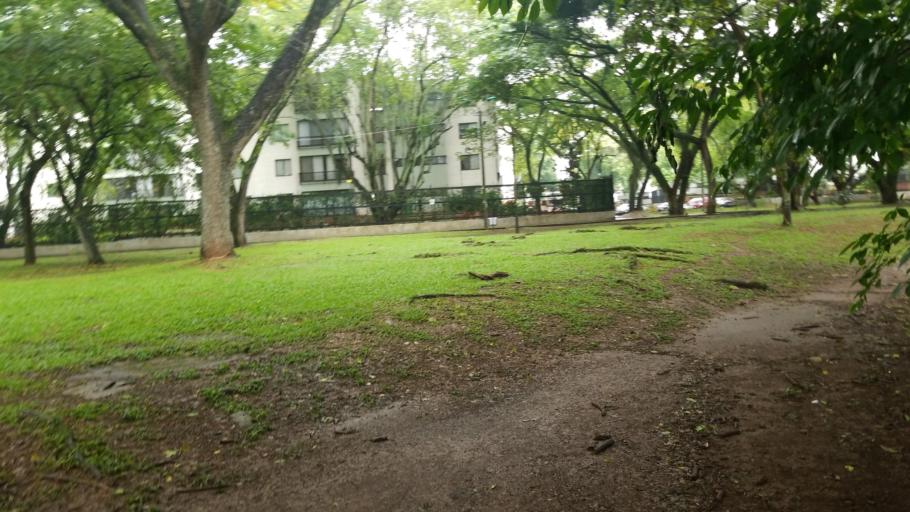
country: CO
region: Valle del Cauca
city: Cali
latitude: 3.3824
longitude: -76.5388
